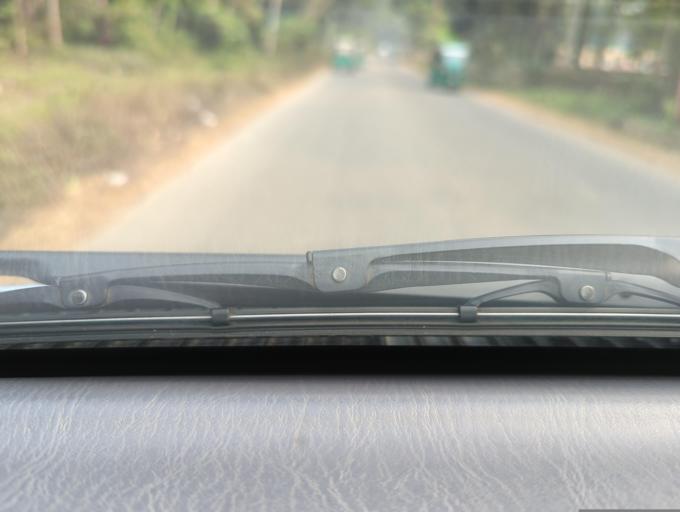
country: BD
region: Sylhet
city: Maulavi Bazar
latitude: 24.4971
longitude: 91.7416
